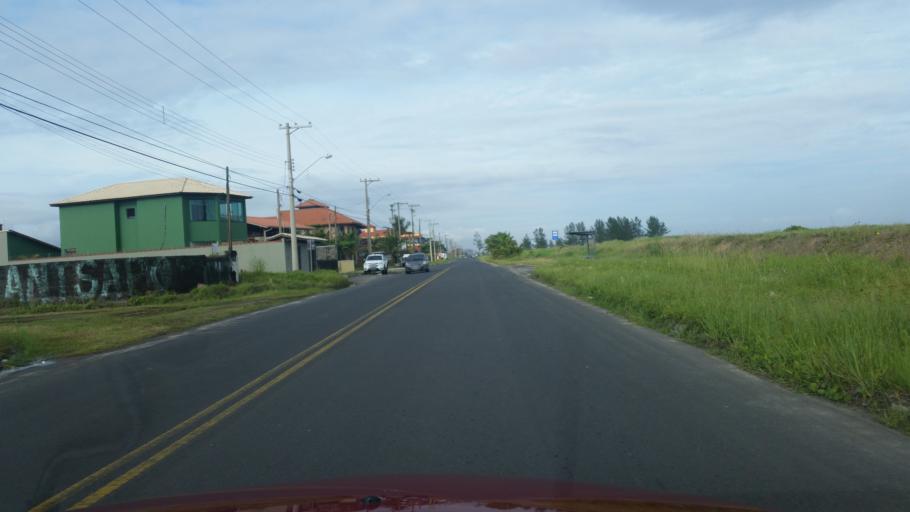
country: BR
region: Sao Paulo
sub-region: Iguape
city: Iguape
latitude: -24.7654
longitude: -47.5776
